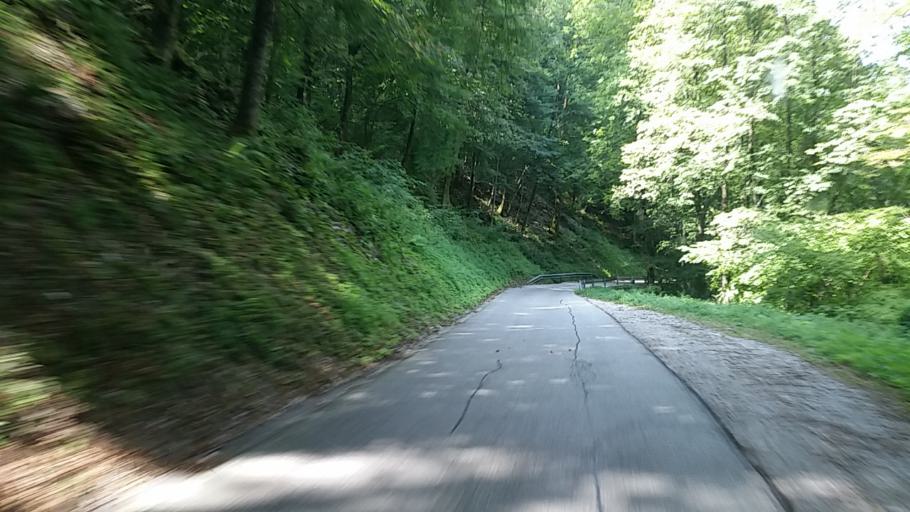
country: SI
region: Tolmin
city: Tolmin
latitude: 46.1267
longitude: 13.7852
